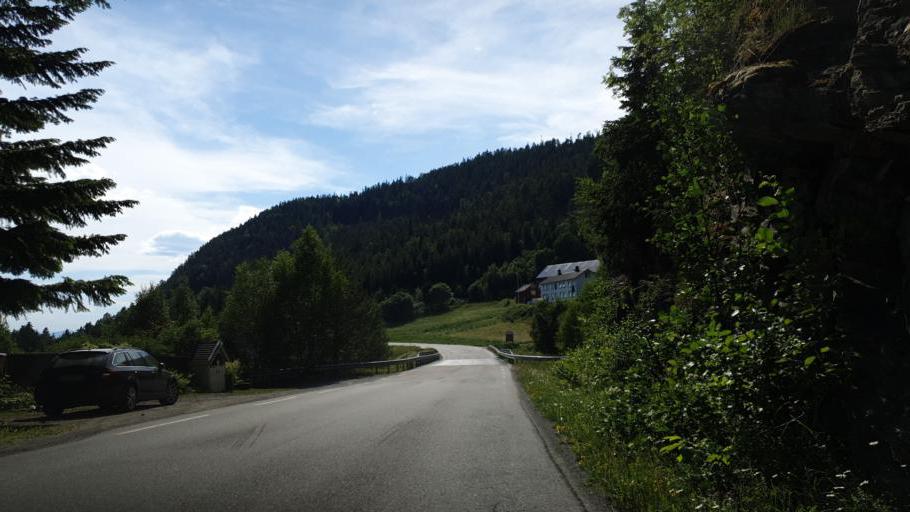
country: NO
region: Nord-Trondelag
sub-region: Leksvik
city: Leksvik
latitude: 63.6356
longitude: 10.5766
